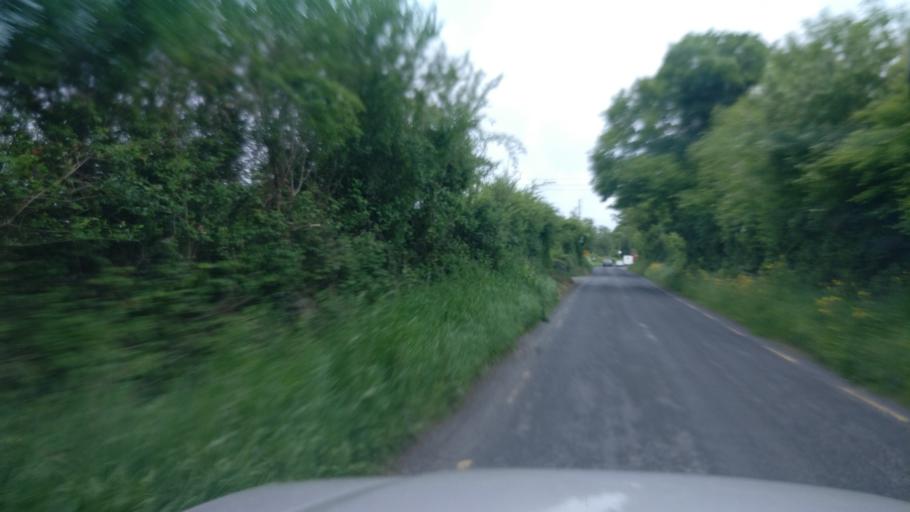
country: IE
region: Connaught
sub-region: County Galway
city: Portumna
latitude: 53.1175
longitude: -8.3089
